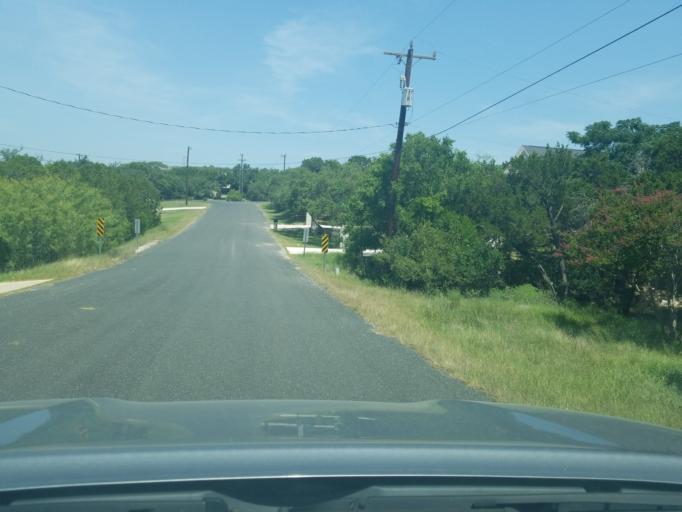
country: US
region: Texas
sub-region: Bexar County
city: Timberwood Park
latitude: 29.6668
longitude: -98.5159
